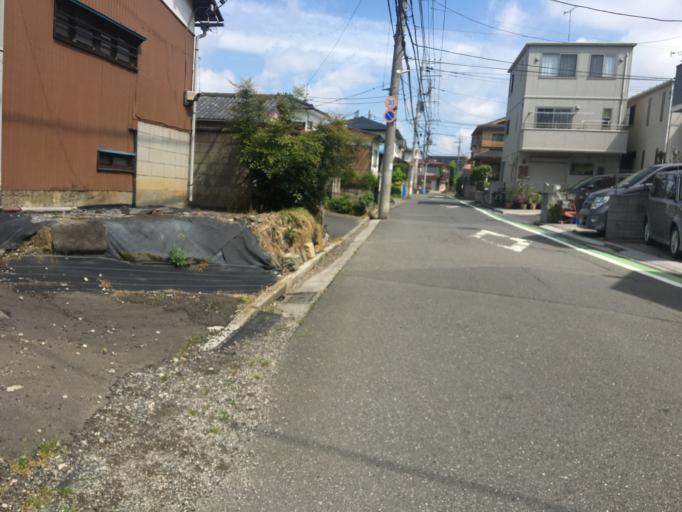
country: JP
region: Saitama
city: Yono
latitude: 35.8664
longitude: 139.6030
